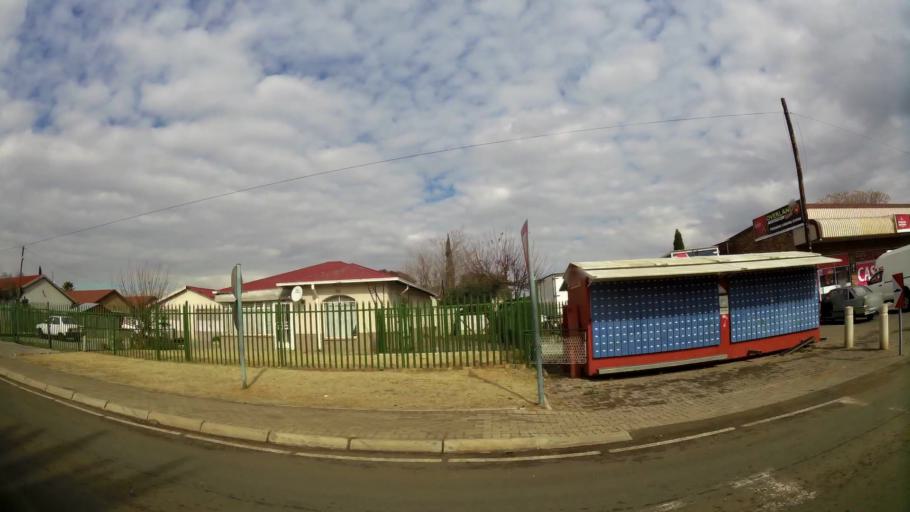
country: ZA
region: Gauteng
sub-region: Sedibeng District Municipality
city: Meyerton
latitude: -26.5988
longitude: 28.0427
